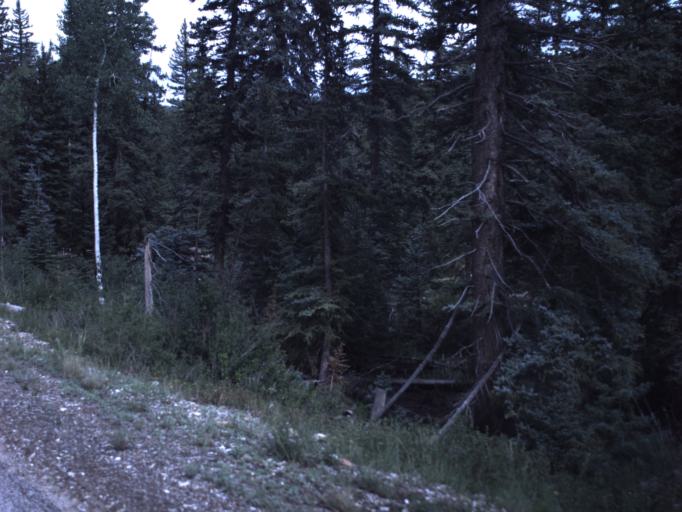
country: US
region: Utah
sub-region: Iron County
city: Cedar City
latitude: 37.5905
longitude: -112.9031
